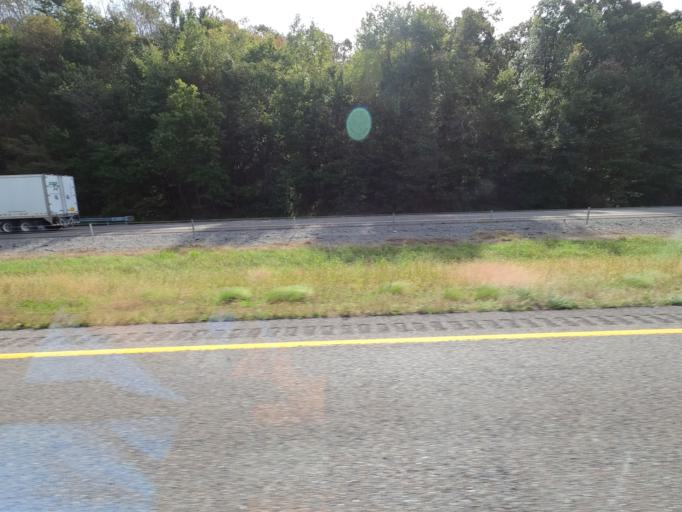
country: US
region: Tennessee
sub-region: Humphreys County
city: New Johnsonville
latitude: 35.8717
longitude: -87.8624
